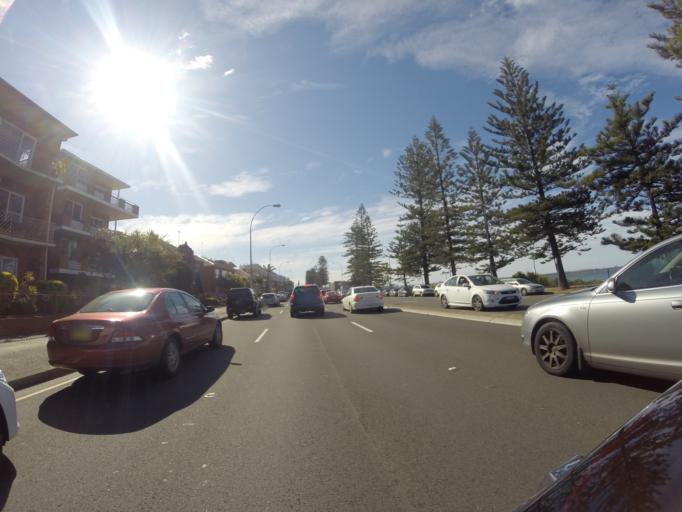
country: AU
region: New South Wales
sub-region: Rockdale
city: Brighton-Le-Sands
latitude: -33.9643
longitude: 151.1548
